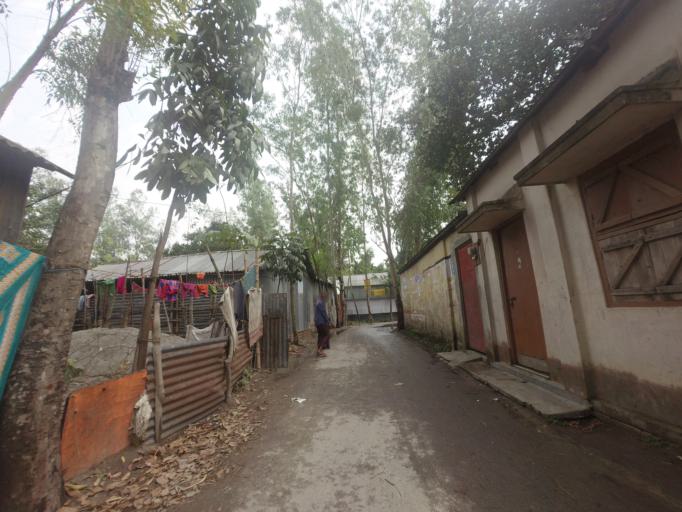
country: BD
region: Rajshahi
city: Sirajganj
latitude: 24.3273
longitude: 89.6944
